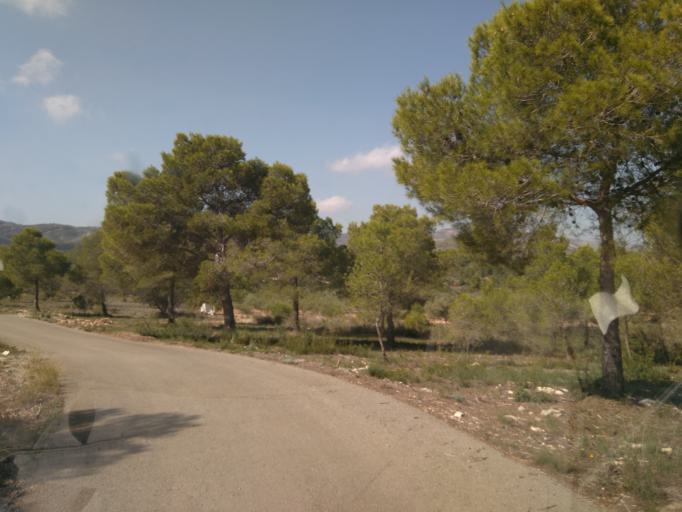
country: ES
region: Valencia
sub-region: Provincia de Valencia
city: Tous
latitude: 39.1752
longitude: -0.6145
